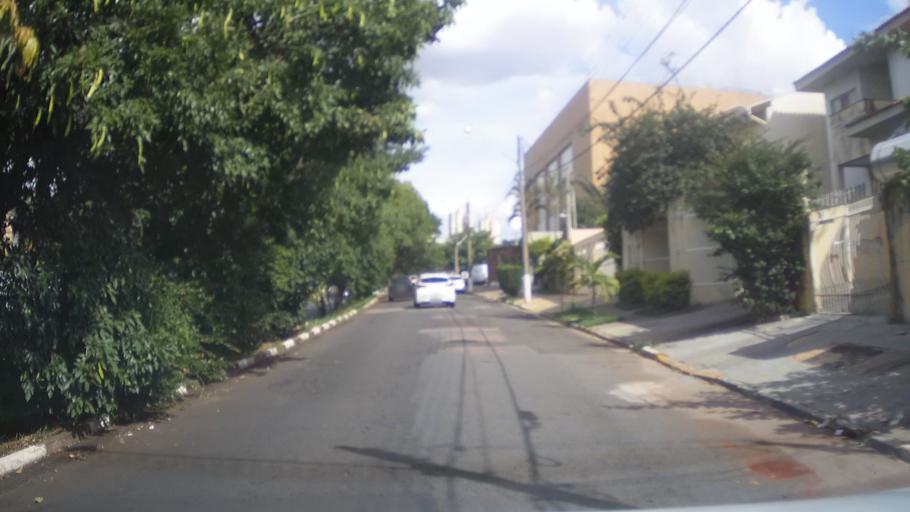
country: BR
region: Sao Paulo
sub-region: Campinas
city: Campinas
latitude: -22.8922
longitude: -47.0915
